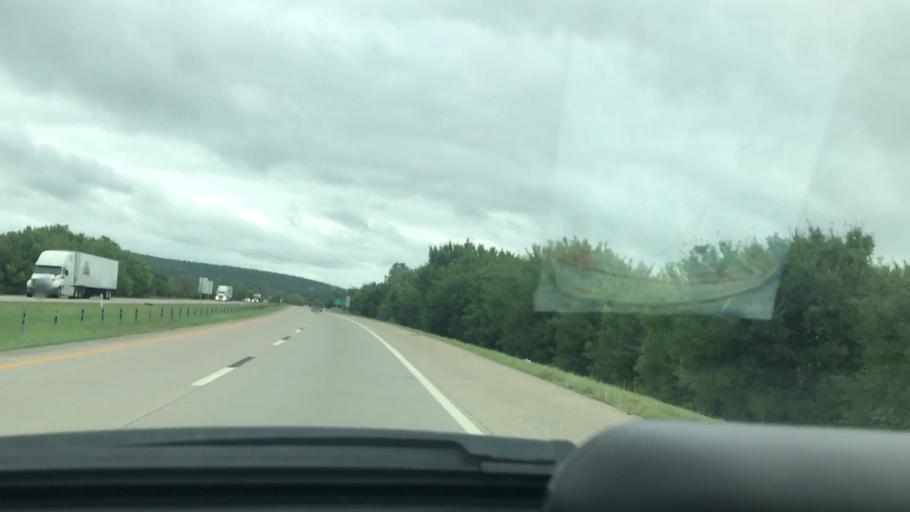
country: US
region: Oklahoma
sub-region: Pittsburg County
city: Krebs
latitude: 35.0075
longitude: -95.7187
